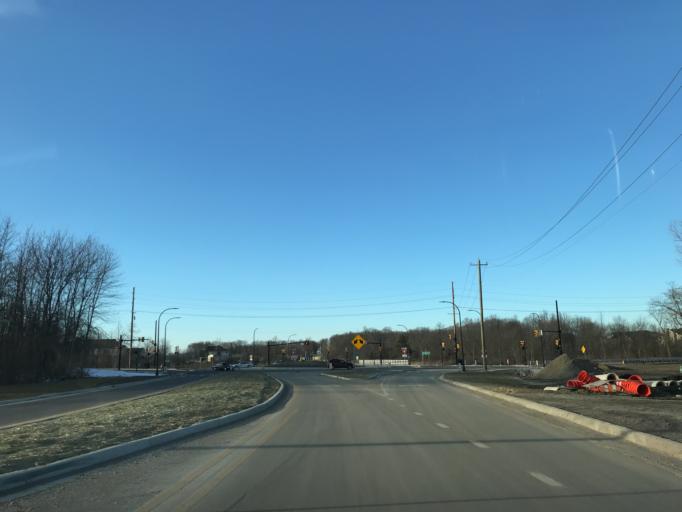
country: US
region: Michigan
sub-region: Oakland County
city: Wixom
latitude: 42.4627
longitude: -83.5534
